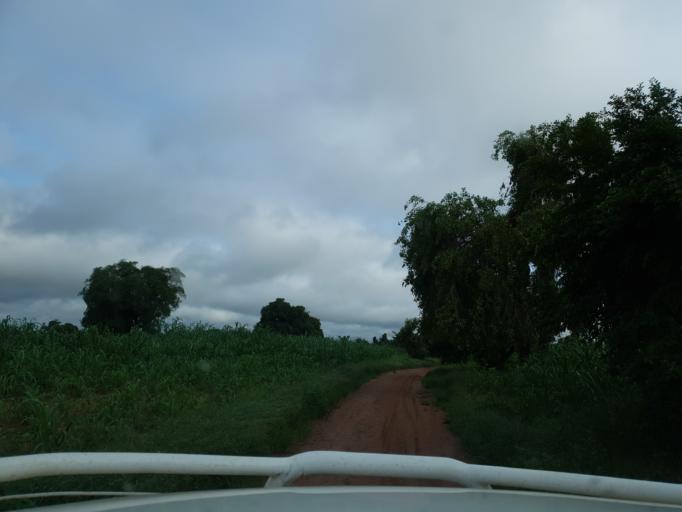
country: ML
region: Segou
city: Baroueli
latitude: 13.4030
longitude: -7.0067
